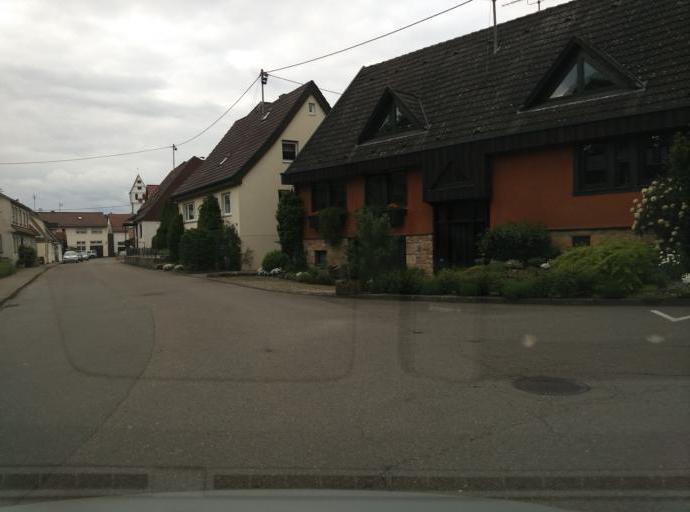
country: DE
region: Baden-Wuerttemberg
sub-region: Regierungsbezirk Stuttgart
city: Frickenhausen
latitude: 48.5901
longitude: 9.3597
